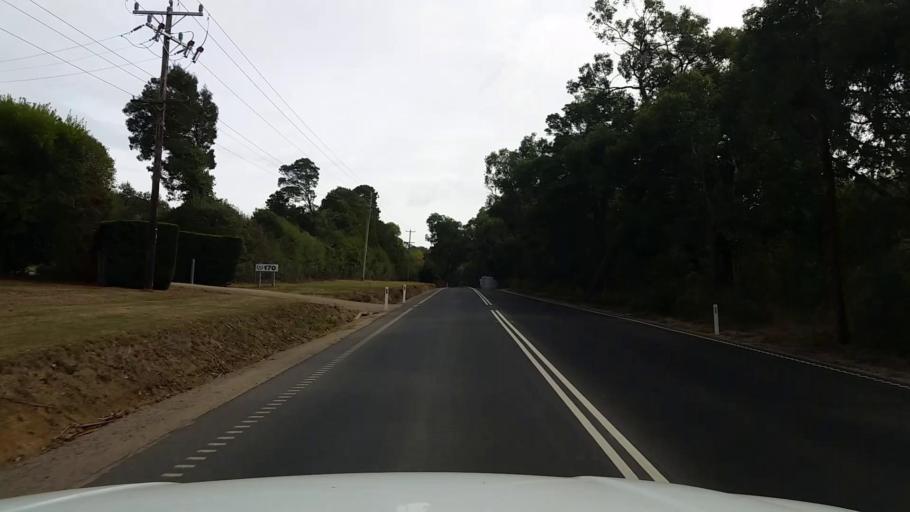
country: AU
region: Victoria
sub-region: Mornington Peninsula
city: Balnarring
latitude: -38.3442
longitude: 145.1008
